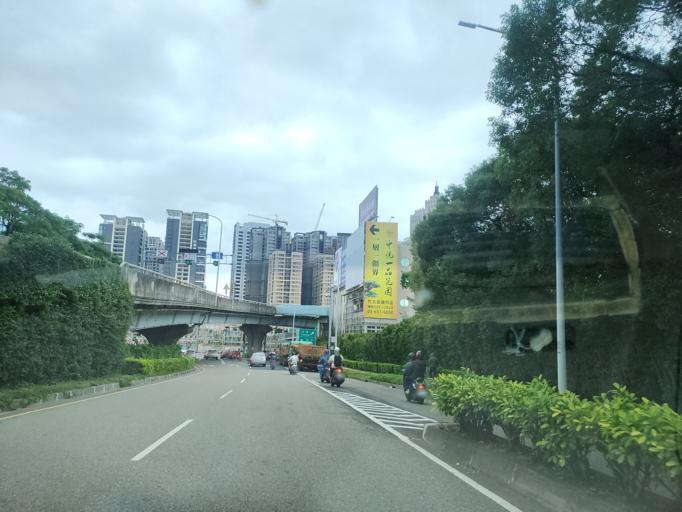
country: TW
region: Taiwan
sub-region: Hsinchu
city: Hsinchu
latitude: 24.7866
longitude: 121.0088
